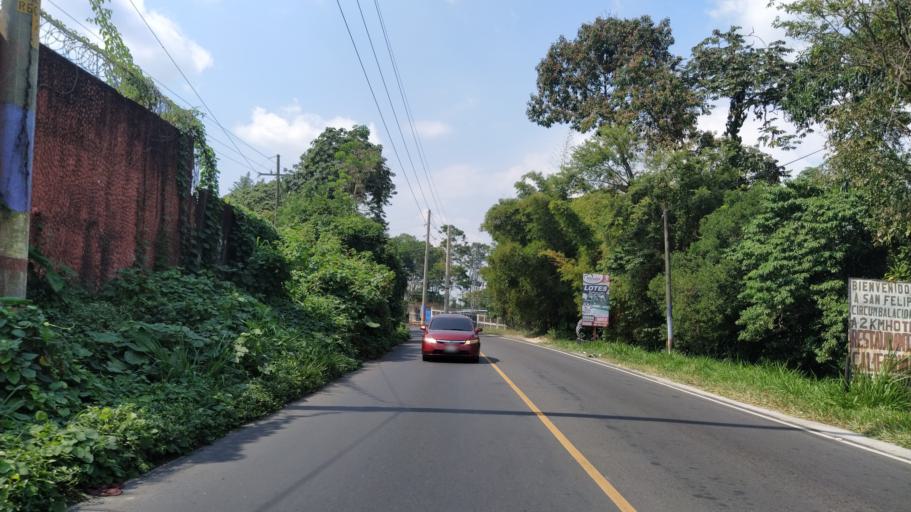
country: GT
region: Quetzaltenango
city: El Palmar
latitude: 14.6333
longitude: -91.5837
